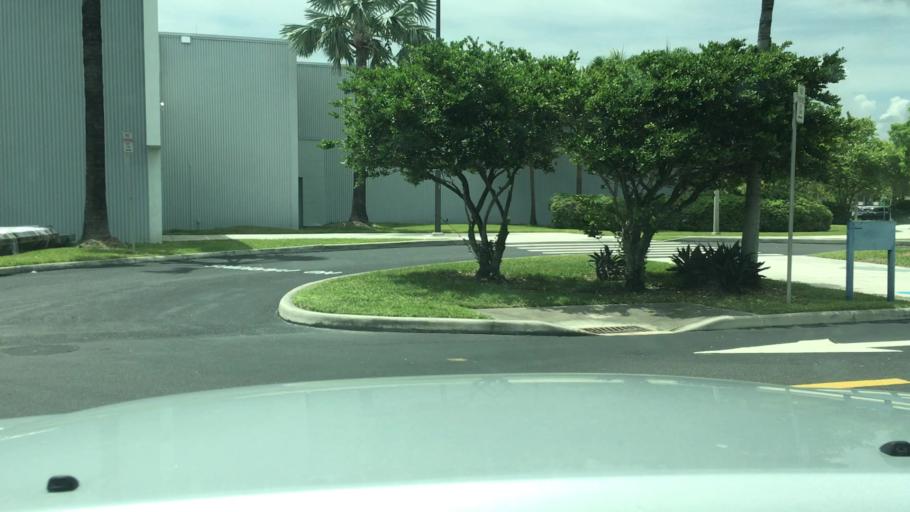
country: US
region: Florida
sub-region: Miami-Dade County
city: Sweetwater
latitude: 25.7802
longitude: -80.3760
